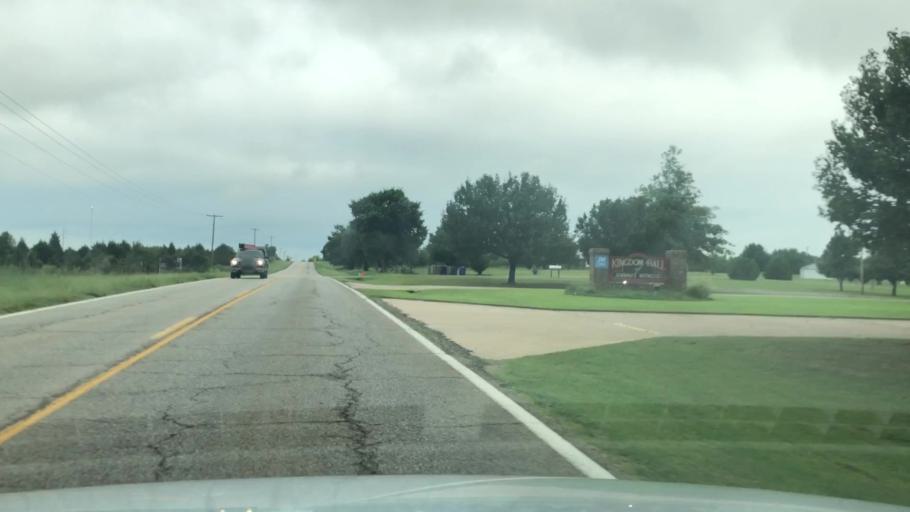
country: US
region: Oklahoma
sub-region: Nowata County
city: Nowata
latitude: 36.7090
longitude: -95.6572
